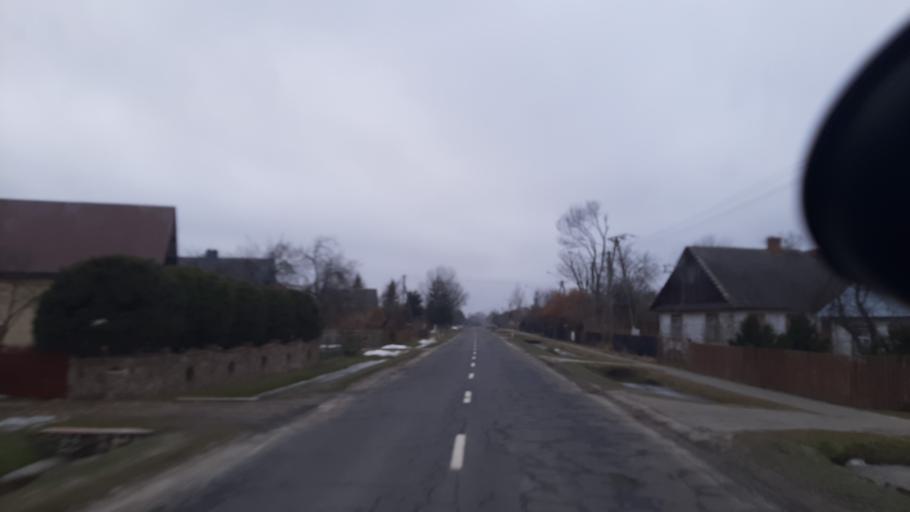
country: PL
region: Lublin Voivodeship
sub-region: Powiat wlodawski
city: Hansk
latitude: 51.5618
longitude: 23.3902
